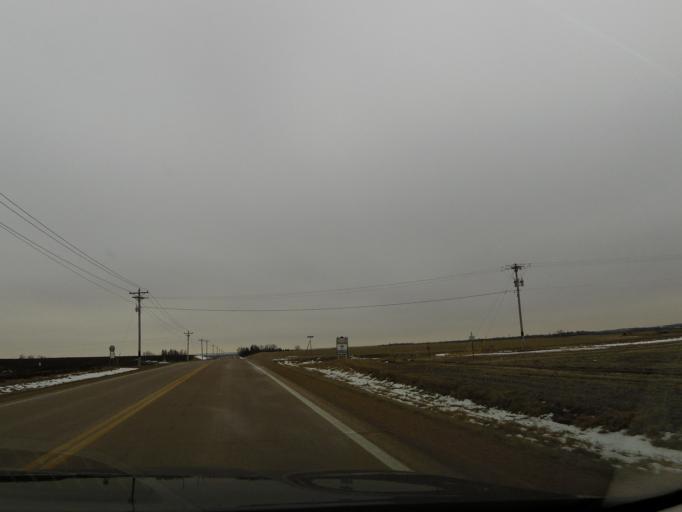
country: US
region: Minnesota
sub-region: Carver County
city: Carver
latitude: 44.7689
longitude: -93.6838
